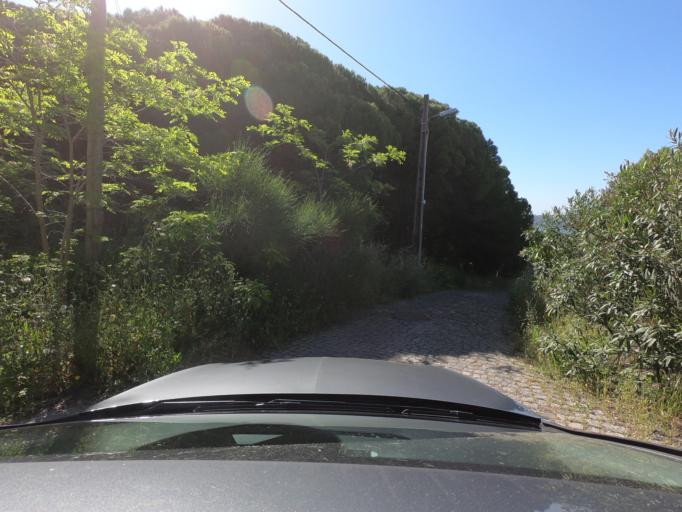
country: PT
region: Lisbon
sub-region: Oeiras
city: Alges
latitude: 38.7045
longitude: -9.2210
